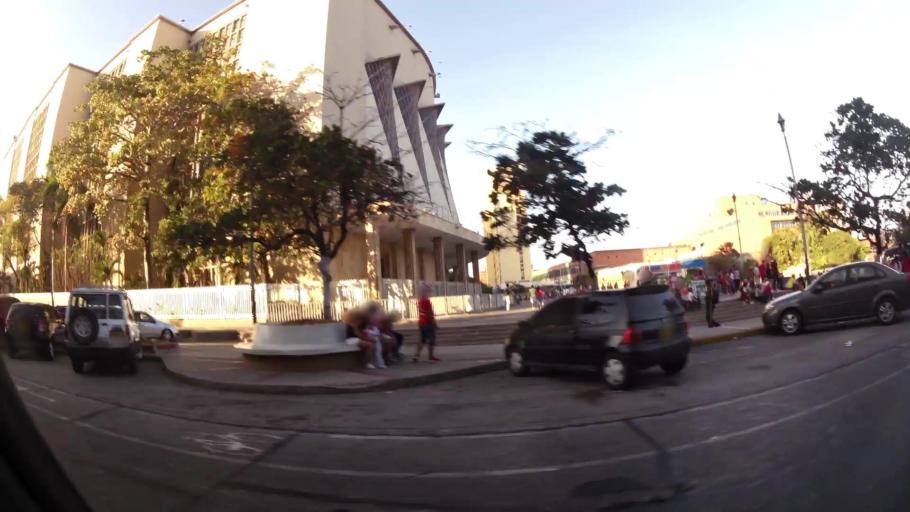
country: CO
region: Atlantico
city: Barranquilla
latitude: 10.9878
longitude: -74.7901
